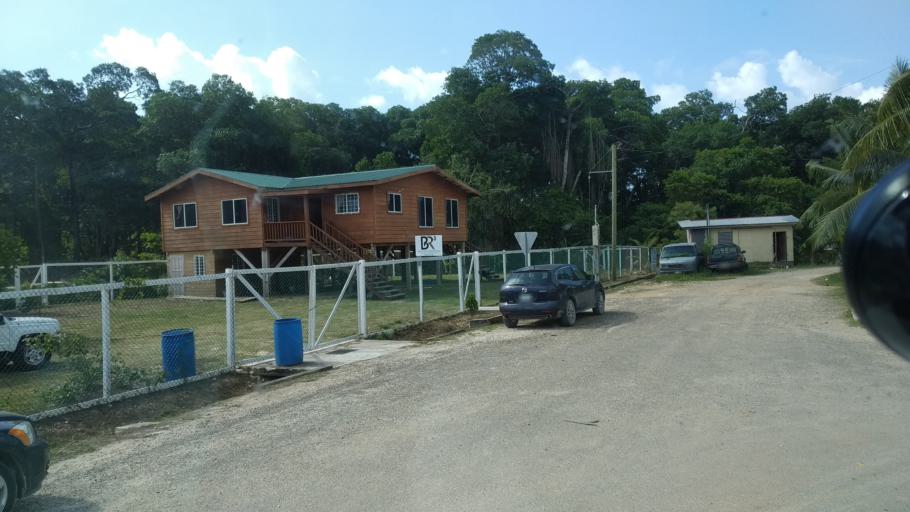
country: BZ
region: Belize
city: Belize City
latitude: 17.5142
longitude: -88.2333
